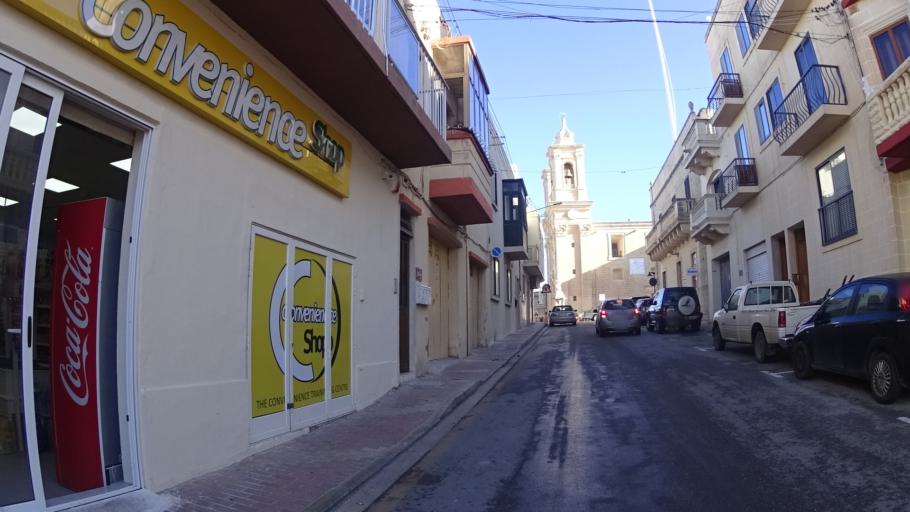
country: MT
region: Hal Gharghur
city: Hal Gharghur
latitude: 35.9233
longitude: 14.4529
